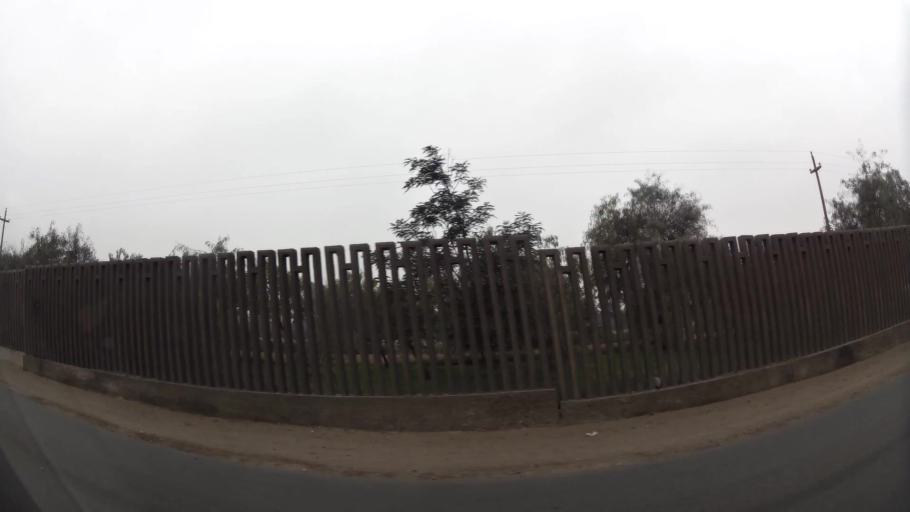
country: PE
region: Lima
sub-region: Lima
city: Vitarte
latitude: -12.0207
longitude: -76.9365
